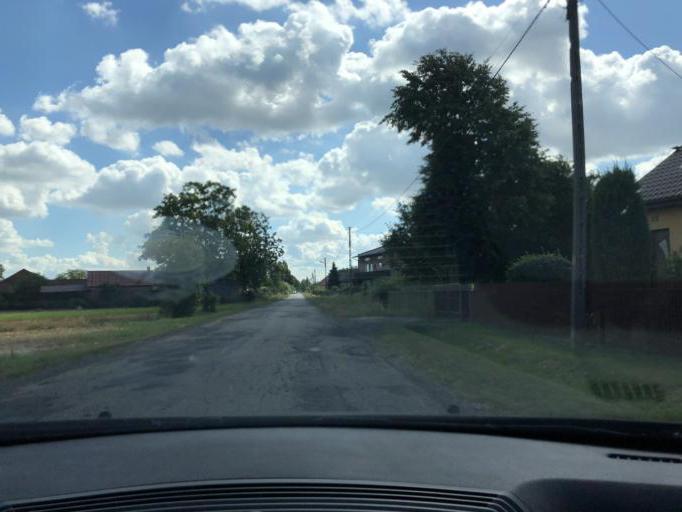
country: PL
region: Lodz Voivodeship
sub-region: Powiat wieruszowski
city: Czastary
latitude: 51.2365
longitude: 18.3433
